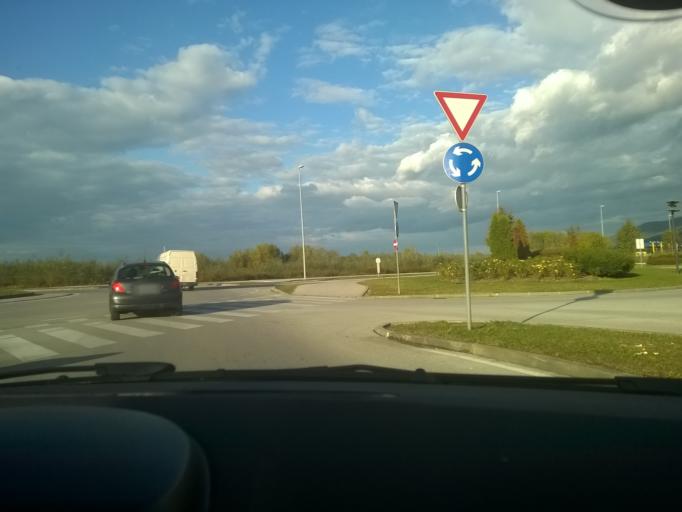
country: HR
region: Zagrebacka
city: Zapresic
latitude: 45.8729
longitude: 15.8254
